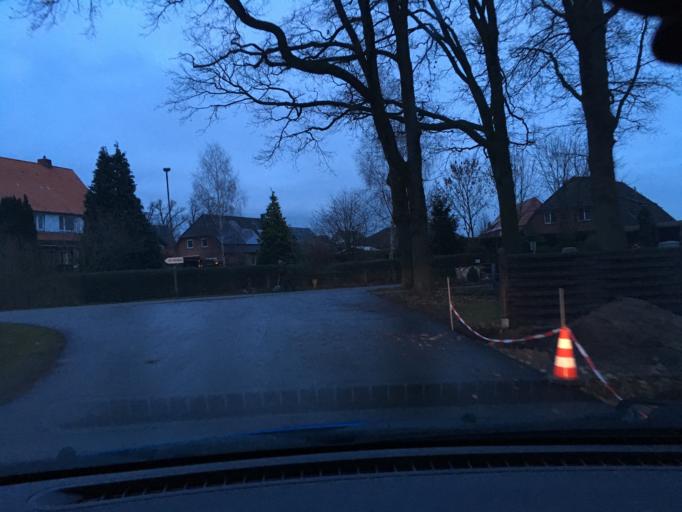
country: DE
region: Lower Saxony
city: Radbruch
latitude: 53.3381
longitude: 10.3140
